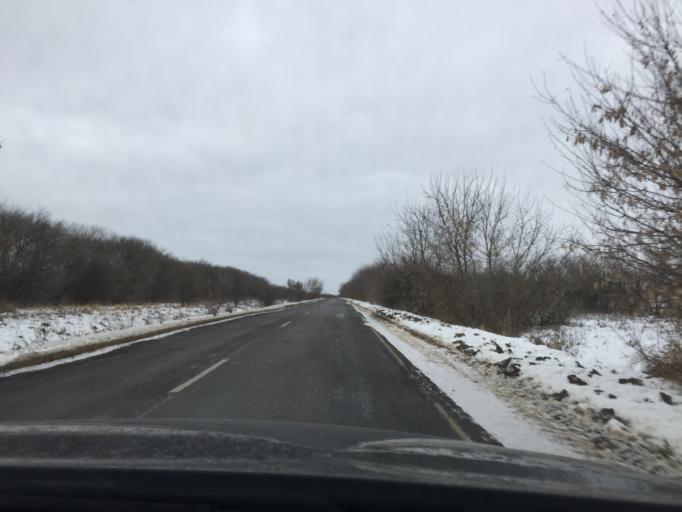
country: RU
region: Tula
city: Teploye
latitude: 53.8043
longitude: 37.5770
